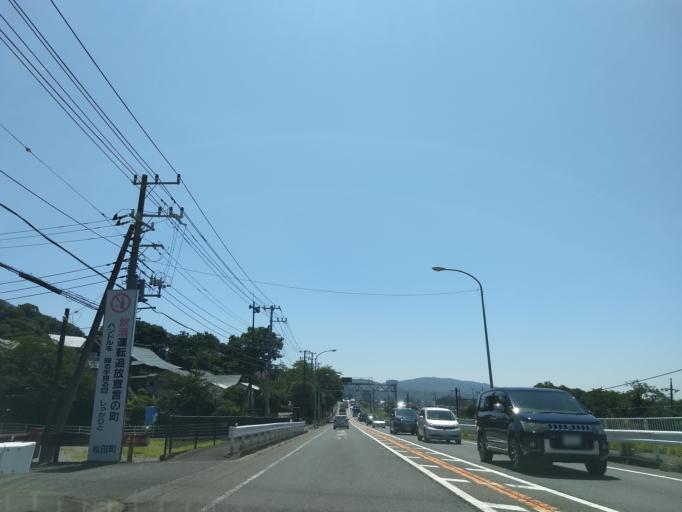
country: JP
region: Kanagawa
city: Odawara
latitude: 35.3528
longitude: 139.1200
